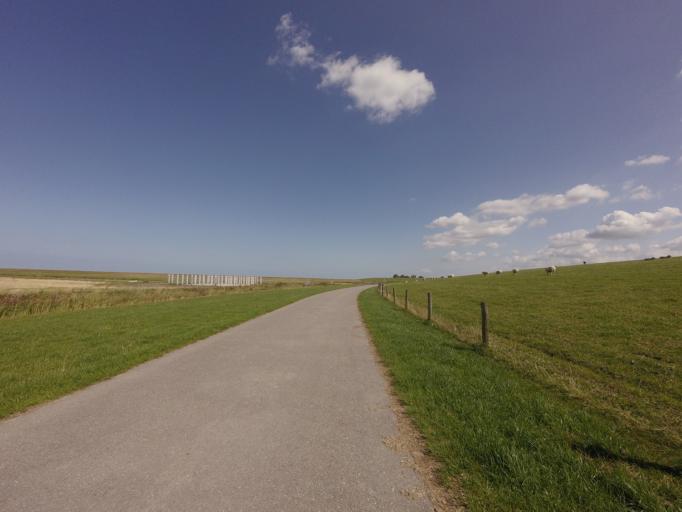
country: NL
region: Friesland
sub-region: Gemeente Ferwerderadiel
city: Marrum
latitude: 53.3380
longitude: 5.7840
